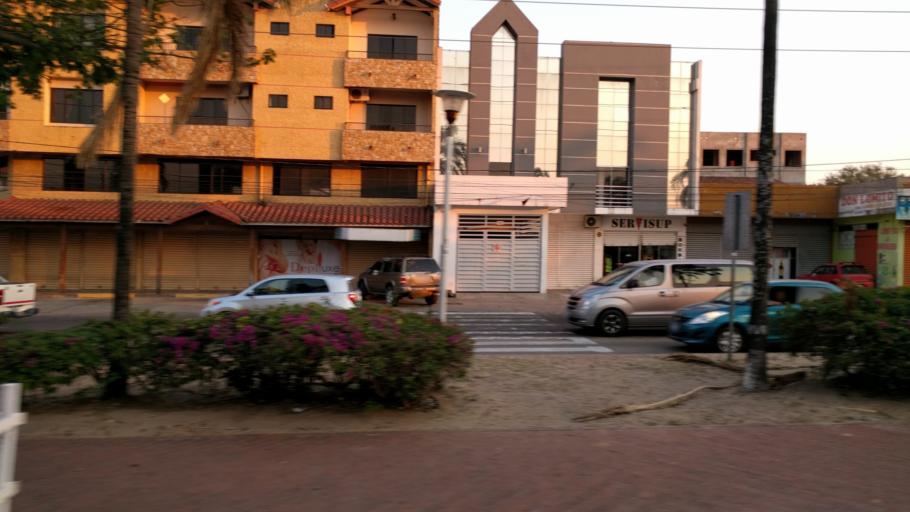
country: BO
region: Santa Cruz
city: Santa Cruz de la Sierra
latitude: -17.7849
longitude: -63.1961
